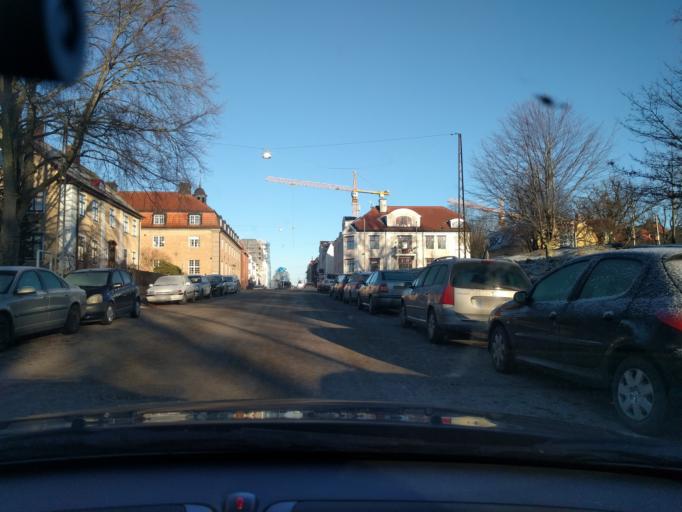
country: SE
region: Kronoberg
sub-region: Vaxjo Kommun
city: Vaexjoe
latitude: 56.8740
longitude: 14.8028
